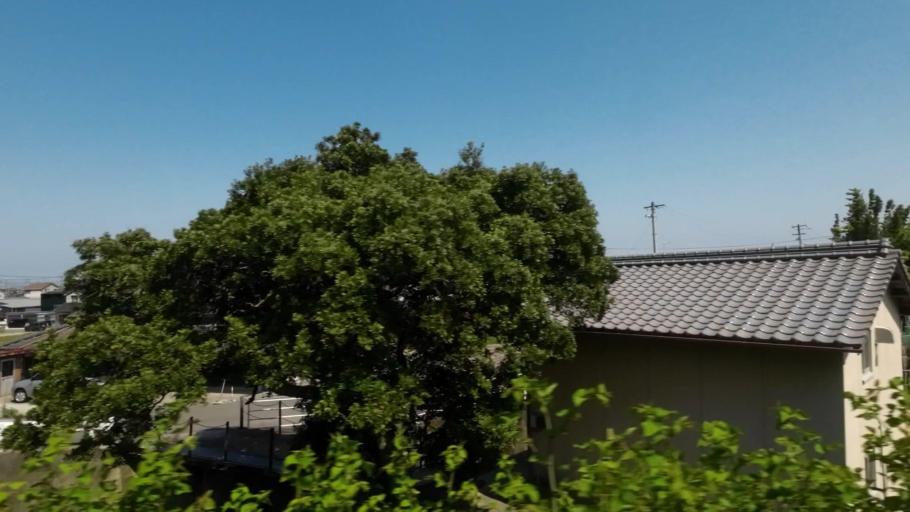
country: JP
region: Ehime
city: Niihama
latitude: 33.9731
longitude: 133.3369
